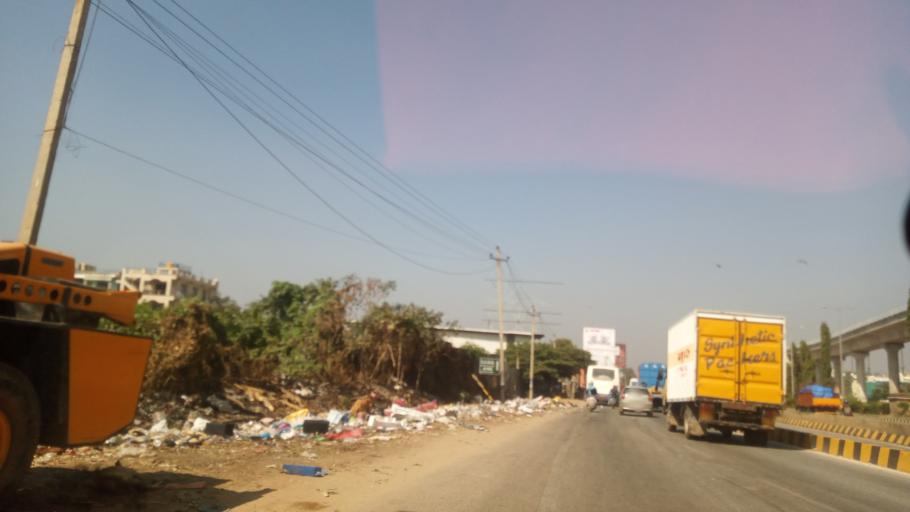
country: IN
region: Karnataka
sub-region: Bangalore Rural
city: Nelamangala
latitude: 13.0509
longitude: 77.4906
